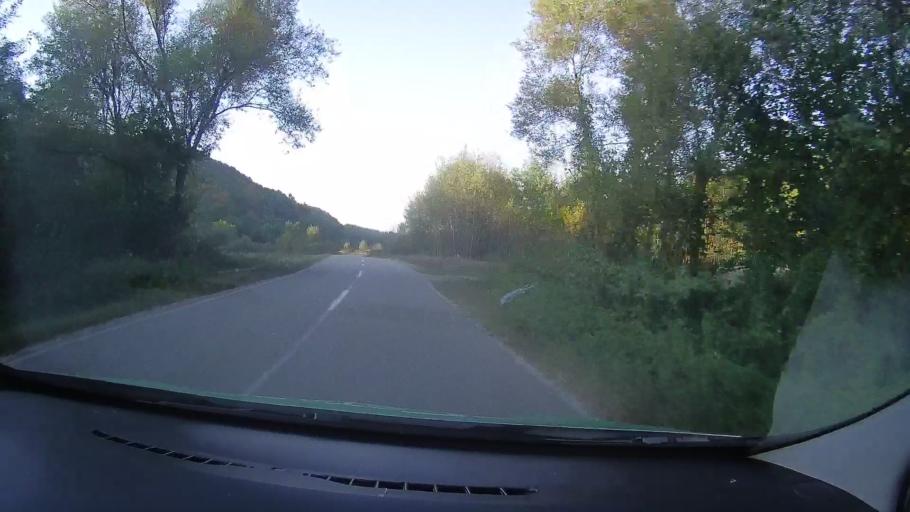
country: RO
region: Timis
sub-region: Comuna Fardea
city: Fardea
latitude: 45.7011
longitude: 22.1607
